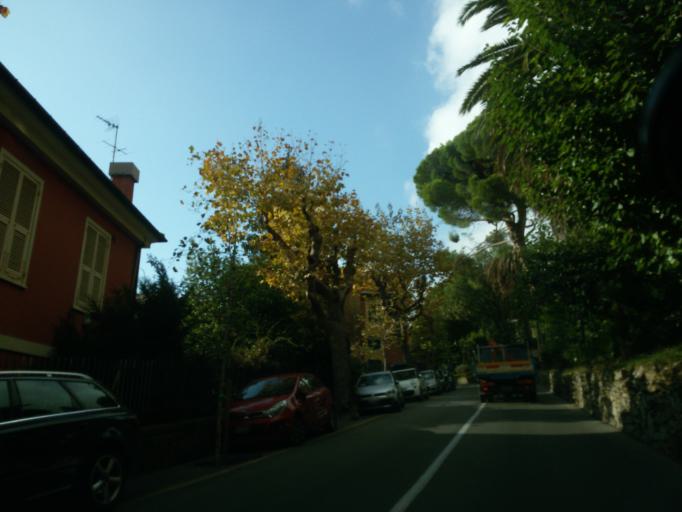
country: IT
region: Liguria
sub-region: Provincia di Genova
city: Camogli
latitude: 44.3483
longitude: 9.1574
